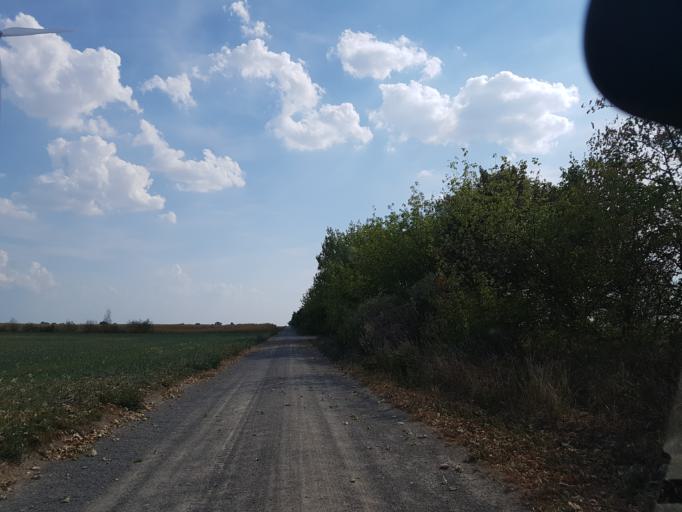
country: DE
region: Brandenburg
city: Treuenbrietzen
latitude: 52.0065
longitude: 12.8689
